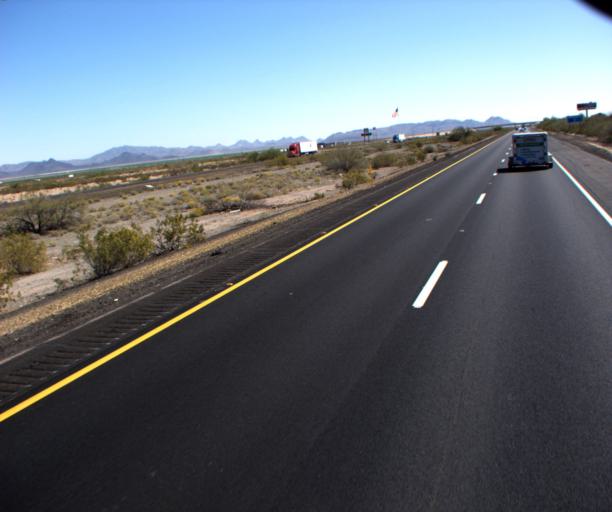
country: US
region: Arizona
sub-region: La Paz County
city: Salome
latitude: 33.6324
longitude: -113.7790
